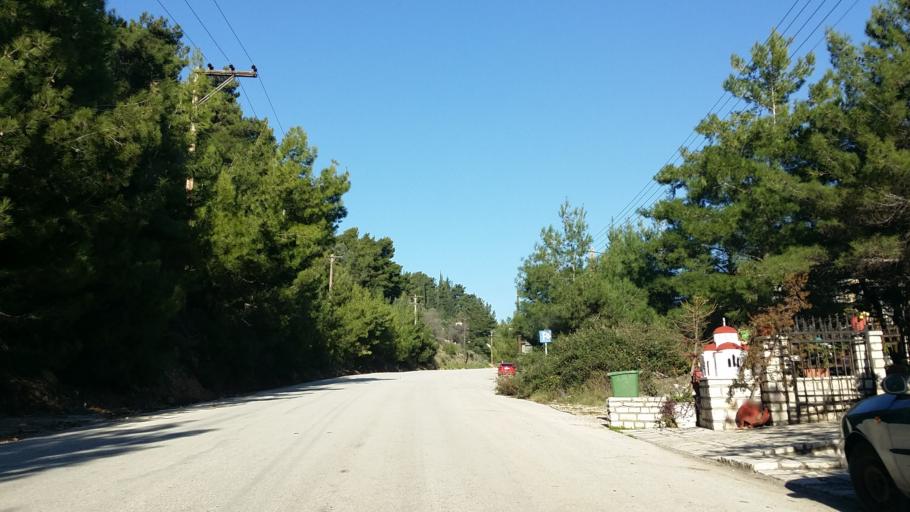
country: GR
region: West Greece
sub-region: Nomos Aitolias kai Akarnanias
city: Astakos
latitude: 38.5337
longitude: 21.0735
